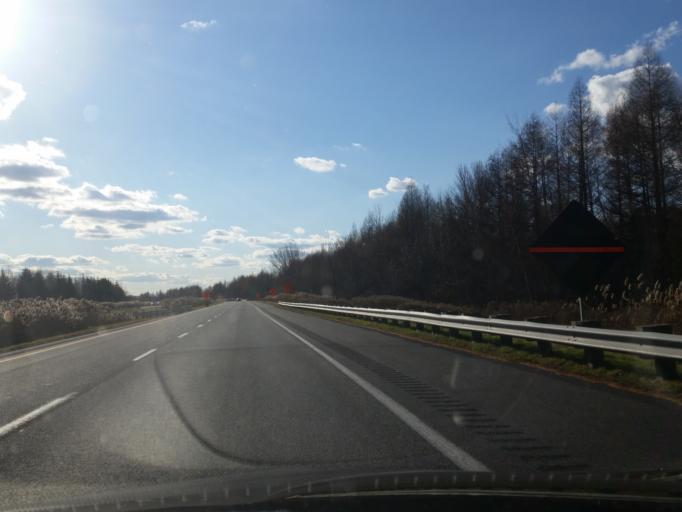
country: CA
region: Quebec
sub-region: Lanaudiere
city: Berthierville
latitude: 46.1141
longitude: -73.1835
